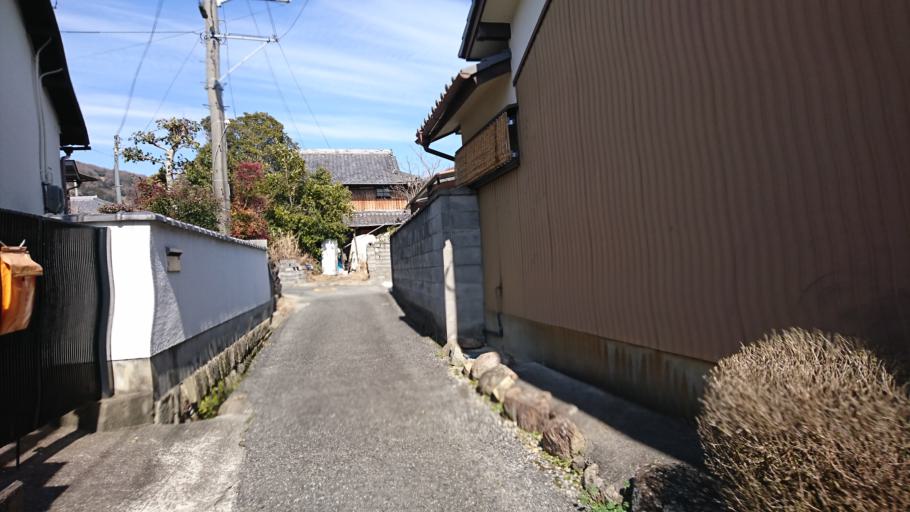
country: JP
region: Hyogo
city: Kakogawacho-honmachi
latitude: 34.8240
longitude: 134.8087
